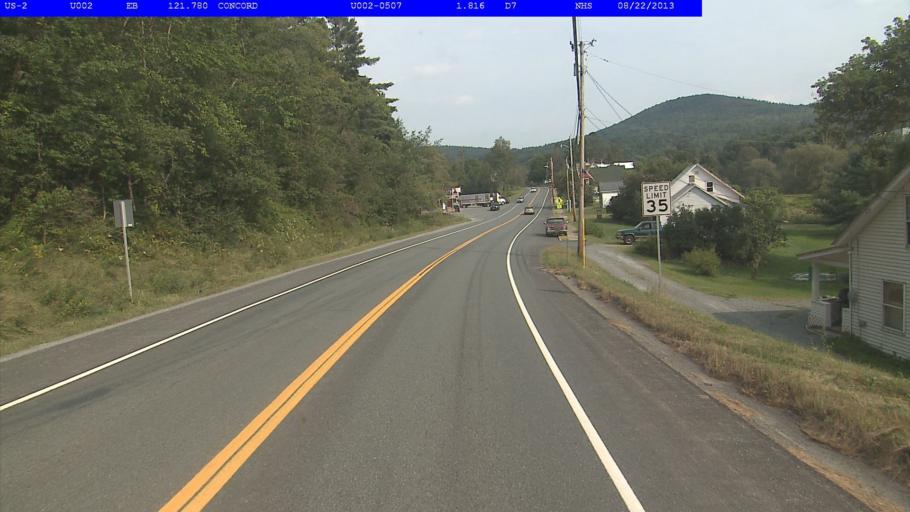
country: US
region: Vermont
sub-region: Caledonia County
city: St Johnsbury
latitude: 44.4301
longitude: -71.8935
